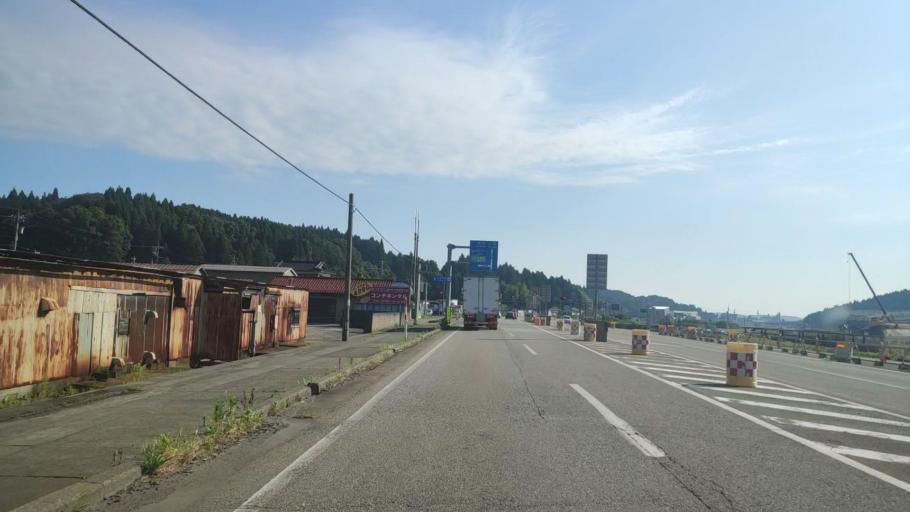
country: JP
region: Fukui
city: Maruoka
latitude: 36.2880
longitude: 136.2955
